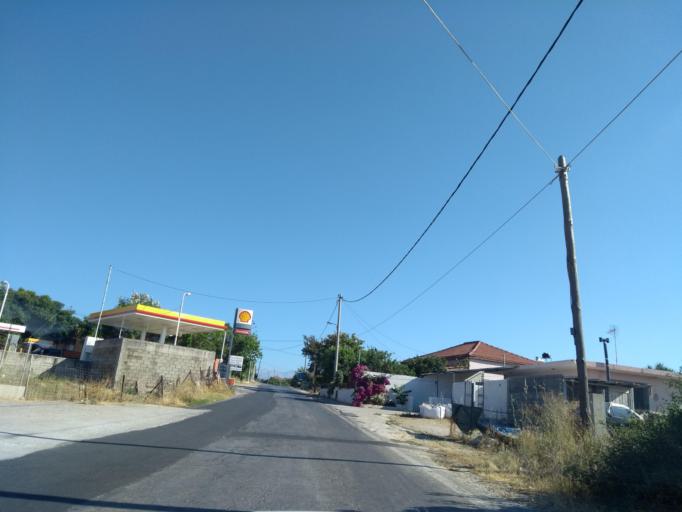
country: GR
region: Crete
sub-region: Nomos Chanias
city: Pithari
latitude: 35.5652
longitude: 24.0919
